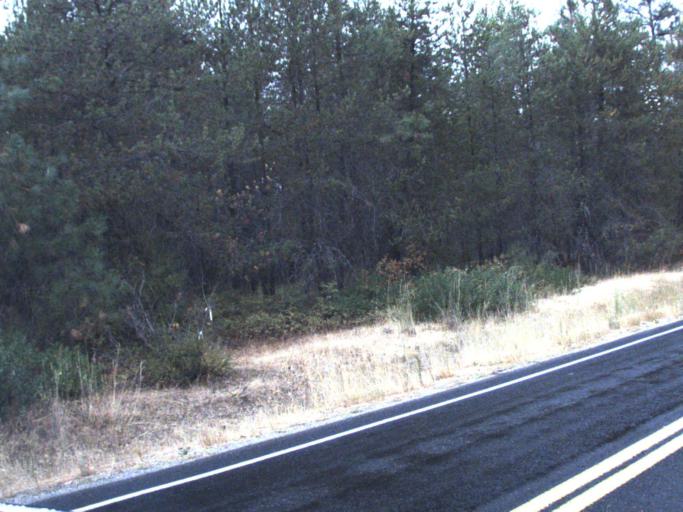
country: US
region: Washington
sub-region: Stevens County
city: Chewelah
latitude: 48.0407
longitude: -117.7372
